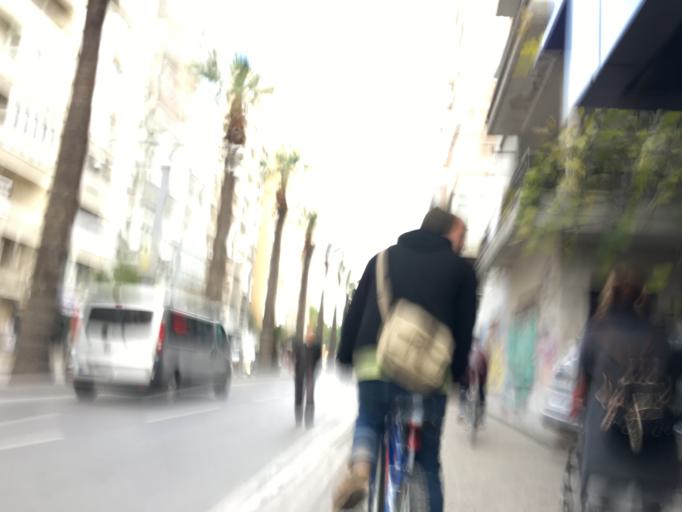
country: TR
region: Izmir
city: Izmir
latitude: 38.4361
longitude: 27.1458
